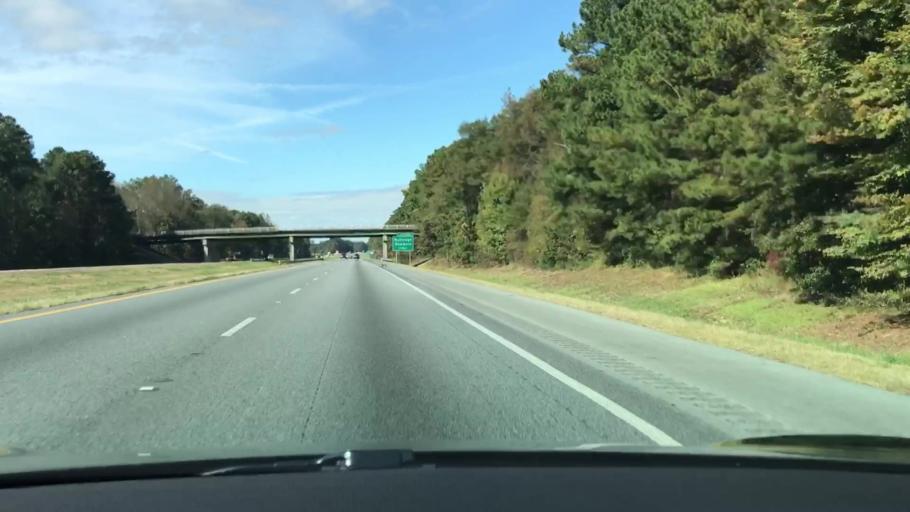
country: US
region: Georgia
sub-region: Walton County
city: Social Circle
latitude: 33.5865
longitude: -83.6083
